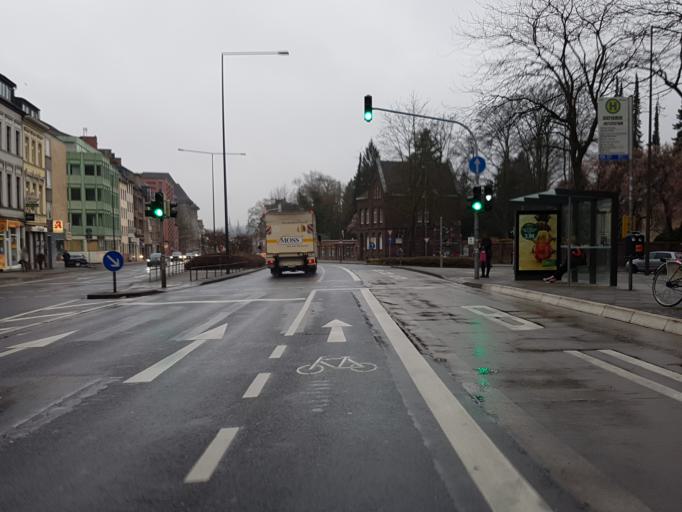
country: DE
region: North Rhine-Westphalia
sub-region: Regierungsbezirk Koln
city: Aachen
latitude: 50.7744
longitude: 6.1077
